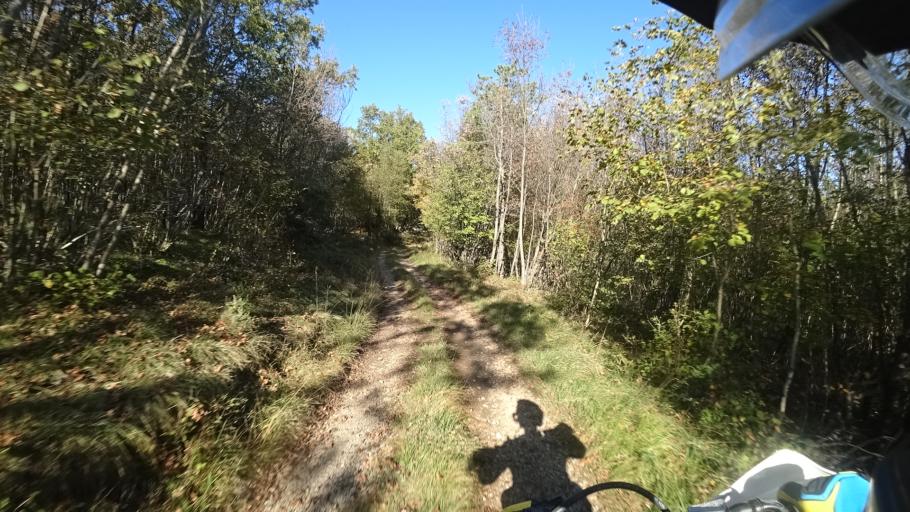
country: HR
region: Primorsko-Goranska
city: Klana
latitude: 45.4506
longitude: 14.3434
